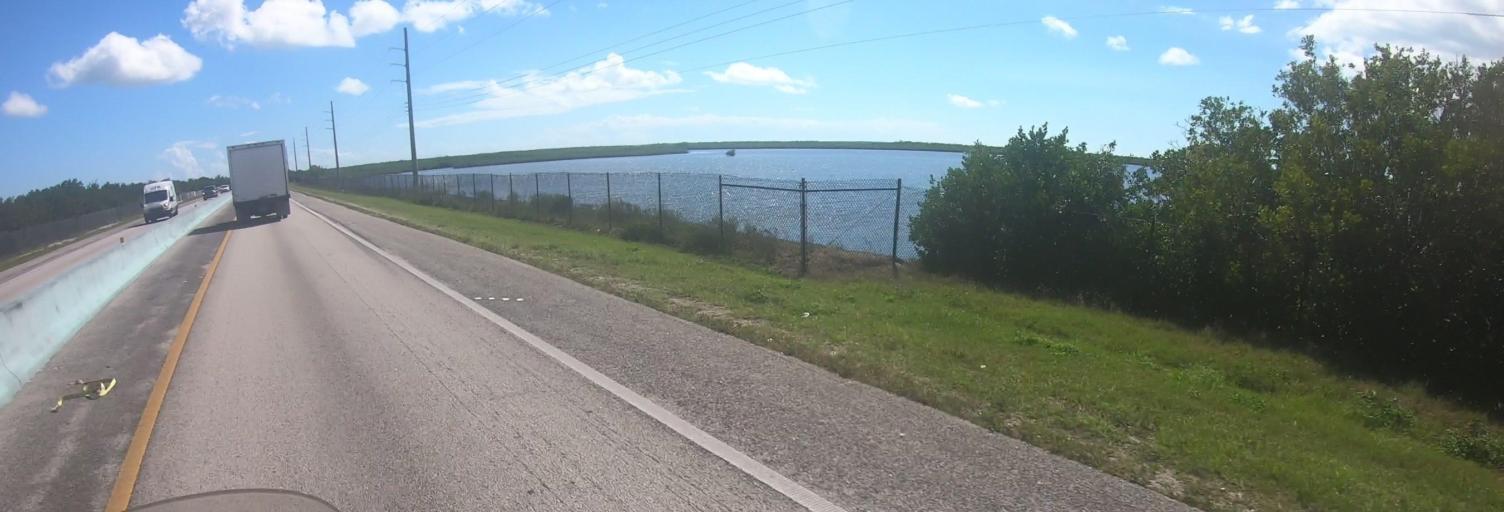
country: US
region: Florida
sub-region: Monroe County
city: North Key Largo
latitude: 25.2498
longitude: -80.4360
